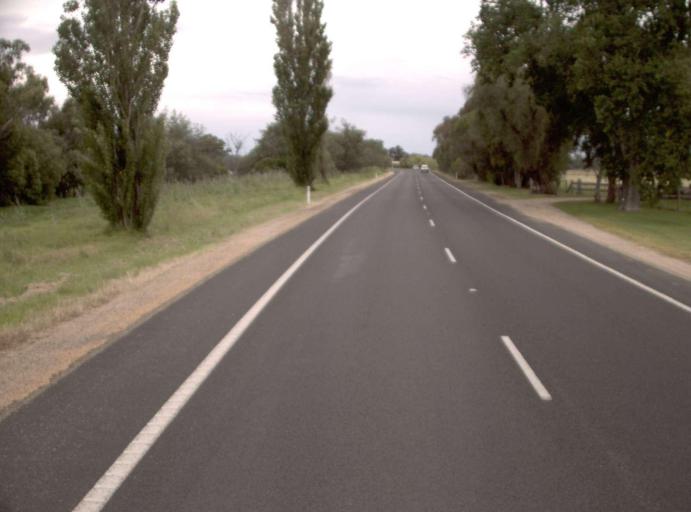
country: AU
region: Victoria
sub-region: East Gippsland
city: Bairnsdale
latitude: -37.8535
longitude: 147.6464
